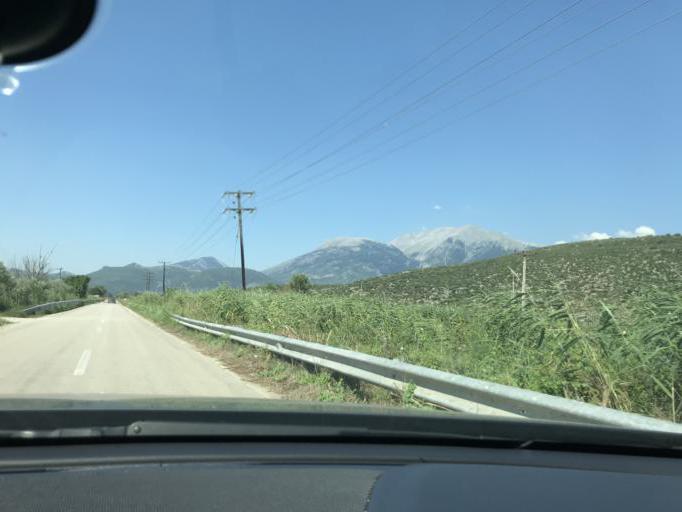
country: GR
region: Central Greece
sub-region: Nomos Fthiotidos
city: Elateia
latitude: 38.5311
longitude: 22.8036
